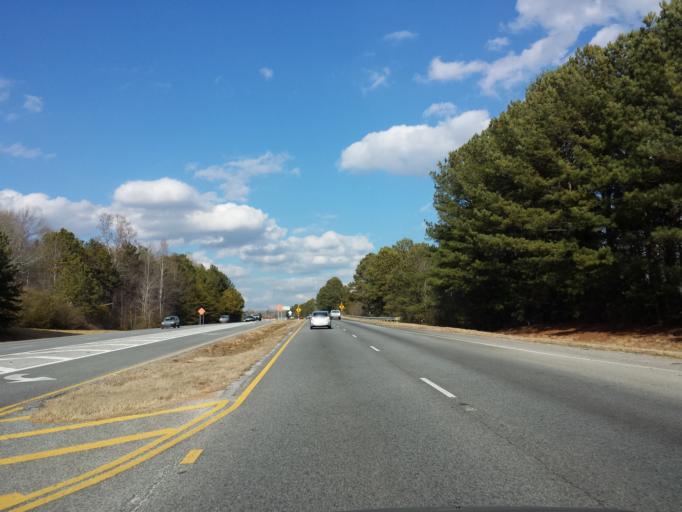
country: US
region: Georgia
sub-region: Dawson County
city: Dawsonville
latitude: 34.3747
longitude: -84.0271
